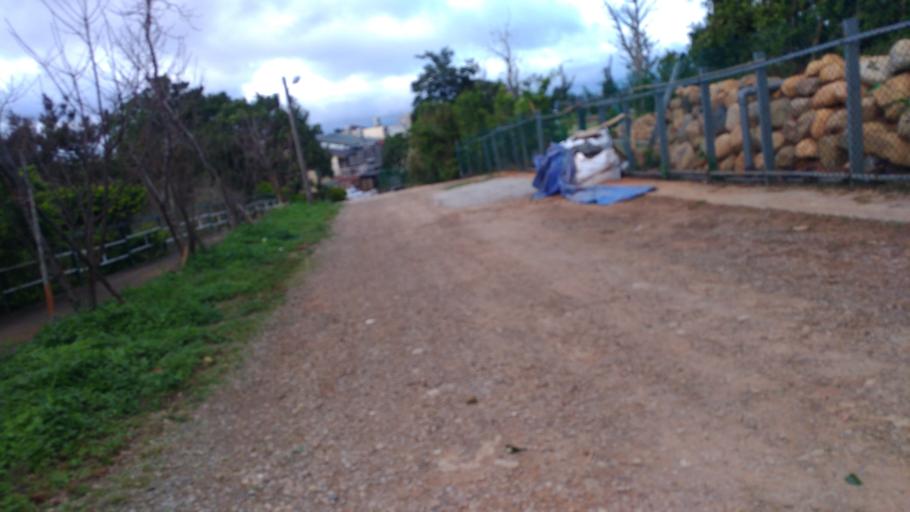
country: TW
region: Taiwan
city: Daxi
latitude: 24.8889
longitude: 121.1711
